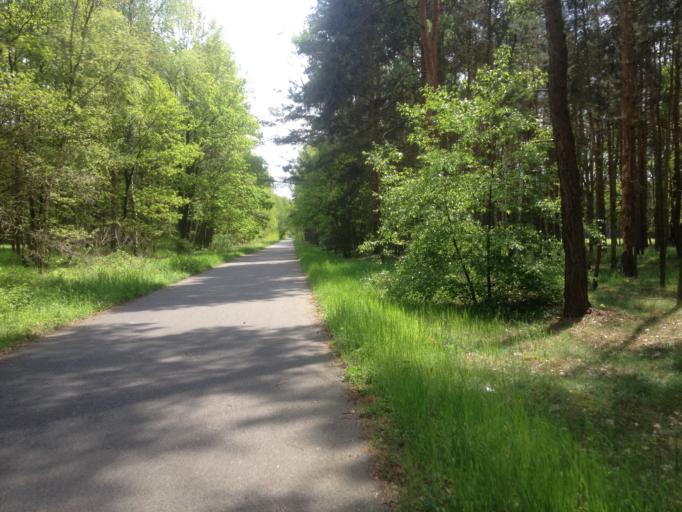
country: DE
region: Brandenburg
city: Briesen
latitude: 51.7988
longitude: 14.2920
